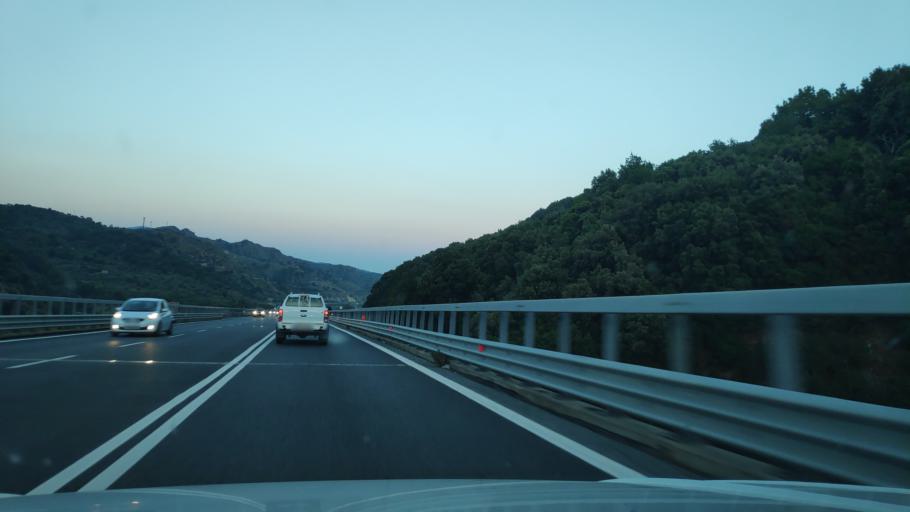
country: IT
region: Calabria
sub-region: Provincia di Reggio Calabria
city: Mammola
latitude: 38.3591
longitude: 16.2126
